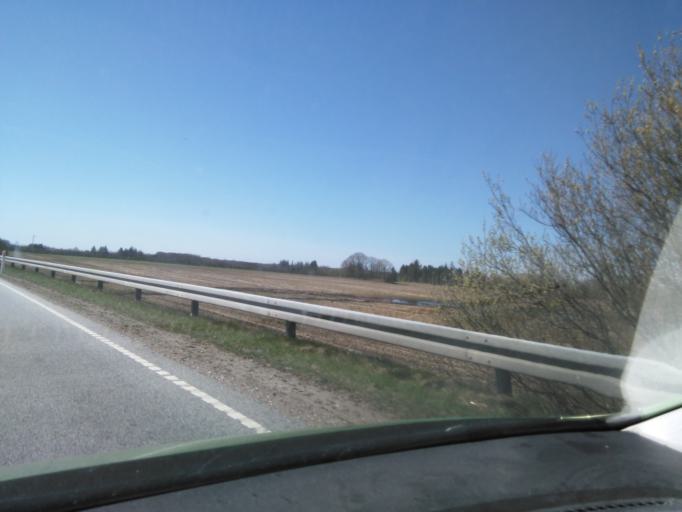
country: DK
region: South Denmark
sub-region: Varde Kommune
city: Varde
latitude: 55.6608
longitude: 8.5612
